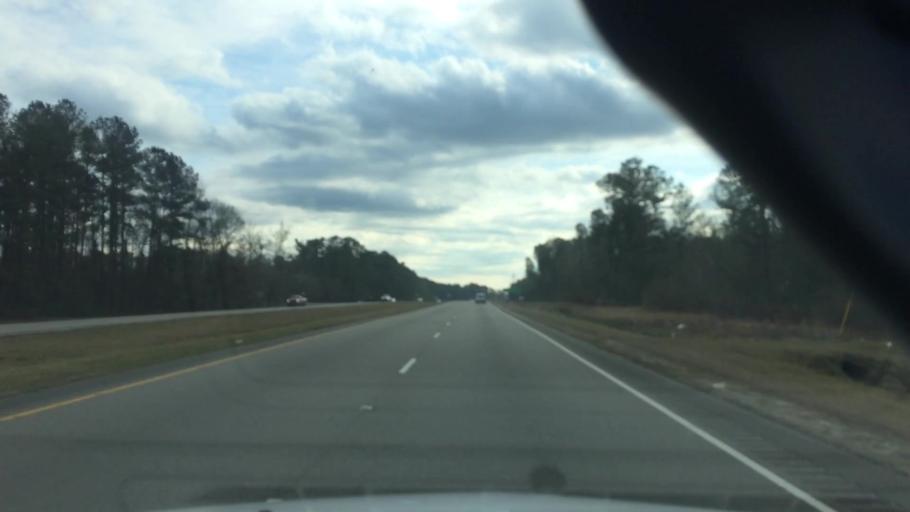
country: US
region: North Carolina
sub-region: Brunswick County
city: Bolivia
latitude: 34.1484
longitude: -78.0940
